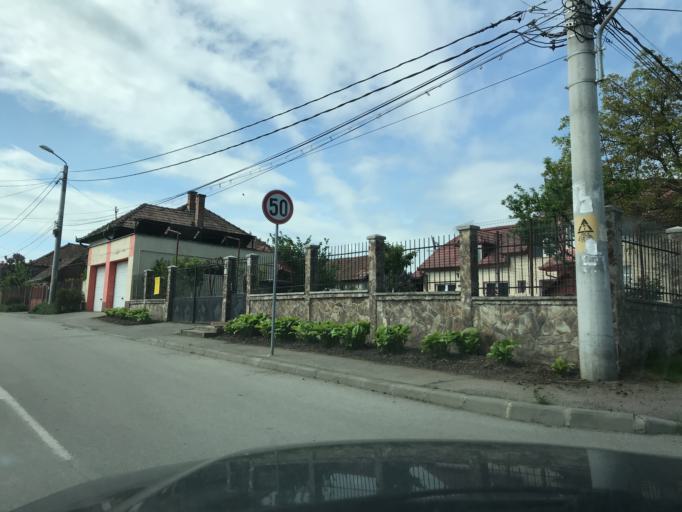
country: RO
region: Cluj
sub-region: Comuna Apahida
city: Sannicoara
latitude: 46.7825
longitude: 23.6700
